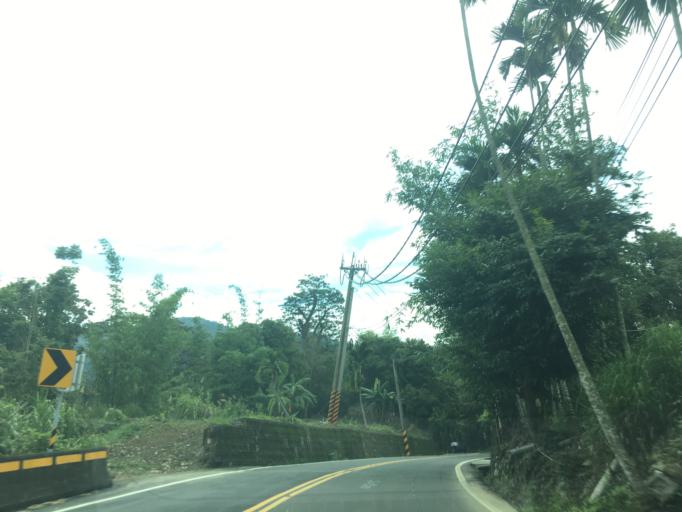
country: TW
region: Taiwan
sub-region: Yunlin
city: Douliu
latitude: 23.5711
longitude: 120.5658
